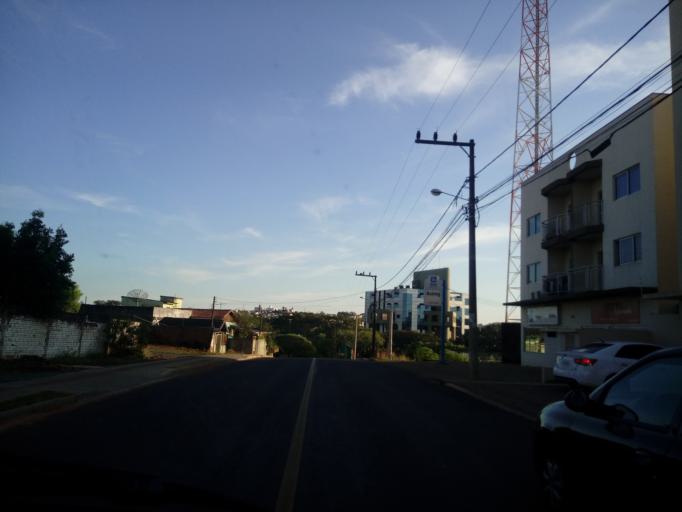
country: BR
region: Santa Catarina
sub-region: Chapeco
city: Chapeco
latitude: -27.0895
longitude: -52.6119
